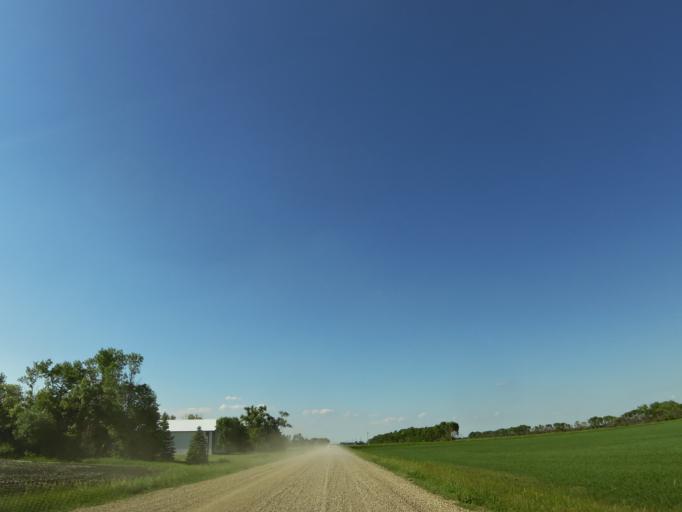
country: US
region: North Dakota
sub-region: Walsh County
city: Grafton
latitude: 48.3513
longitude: -97.2556
